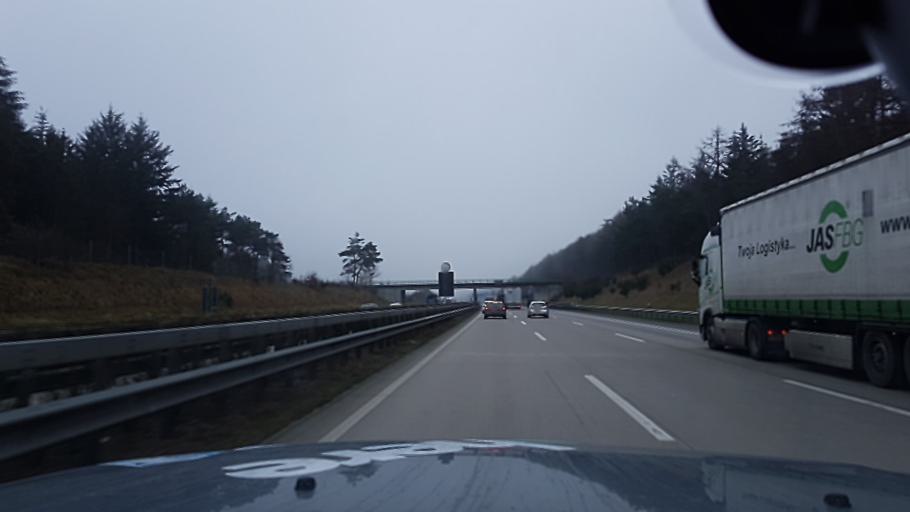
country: DE
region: Lower Saxony
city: Buehren
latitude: 52.8707
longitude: 8.2465
